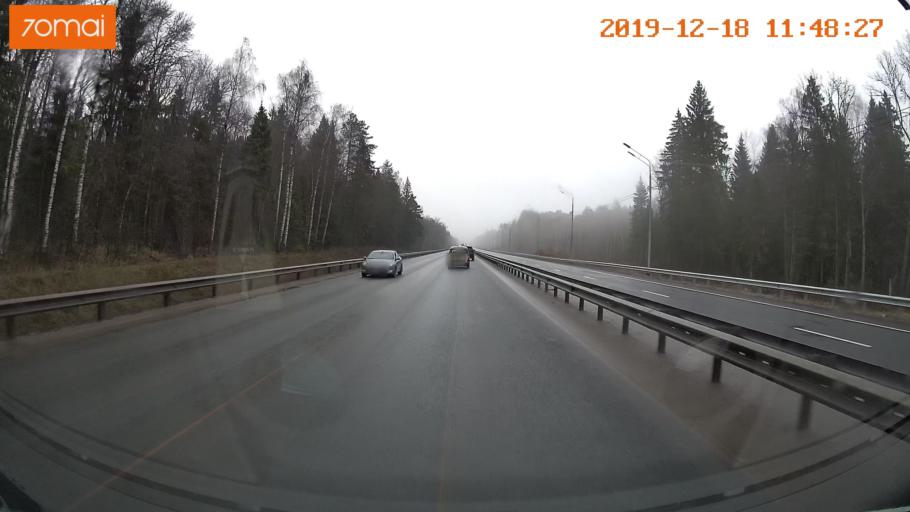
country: RU
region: Moskovskaya
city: Yershovo
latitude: 55.7682
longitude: 36.9036
